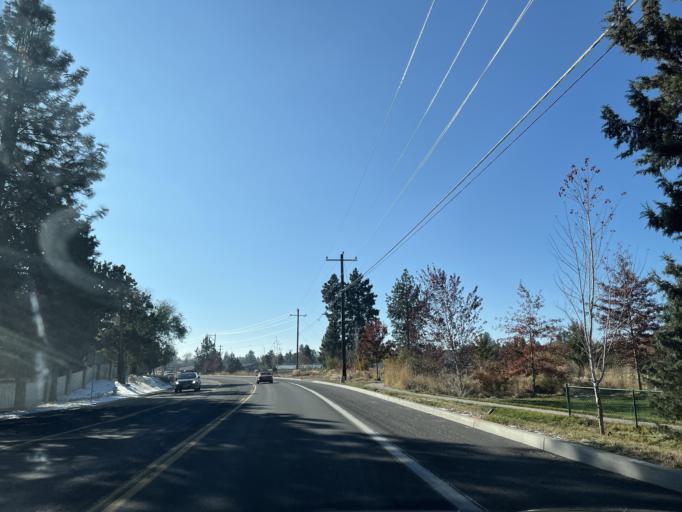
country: US
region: Oregon
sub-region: Deschutes County
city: Bend
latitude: 44.0813
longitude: -121.2808
